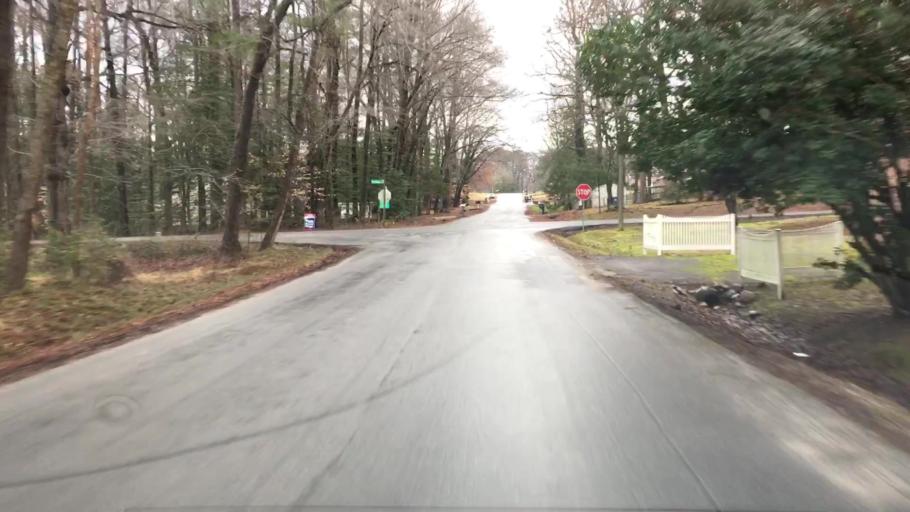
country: US
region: Virginia
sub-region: Chesterfield County
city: Bon Air
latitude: 37.4761
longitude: -77.5901
